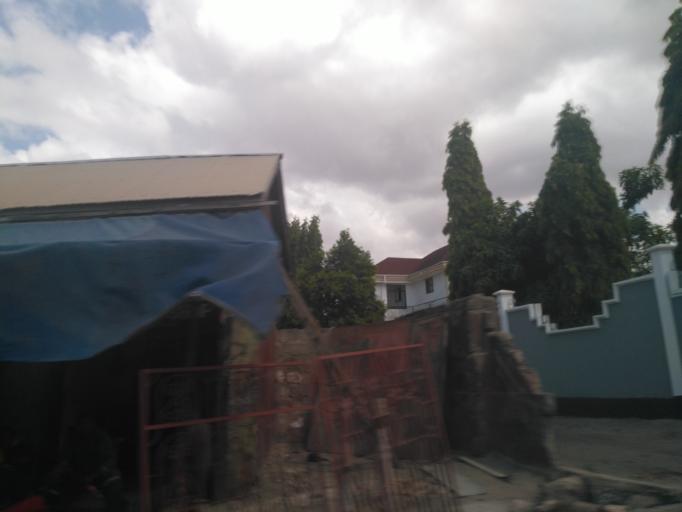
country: TZ
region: Dar es Salaam
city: Dar es Salaam
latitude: -6.8898
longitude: 39.2874
